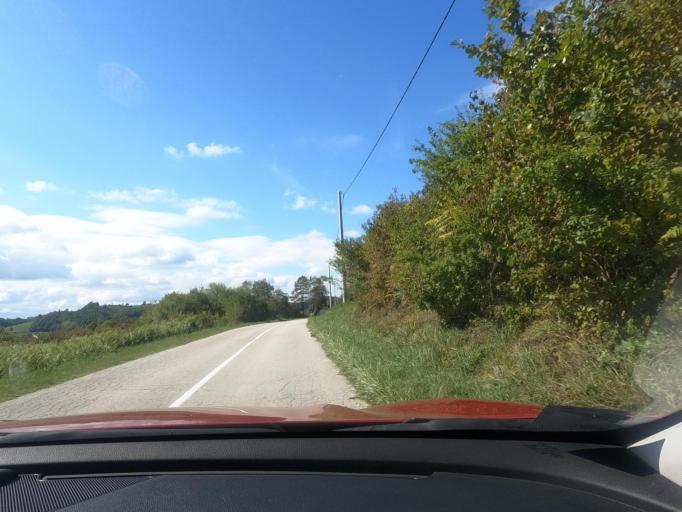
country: BA
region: Federation of Bosnia and Herzegovina
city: Podzvizd
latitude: 45.2251
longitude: 15.8837
